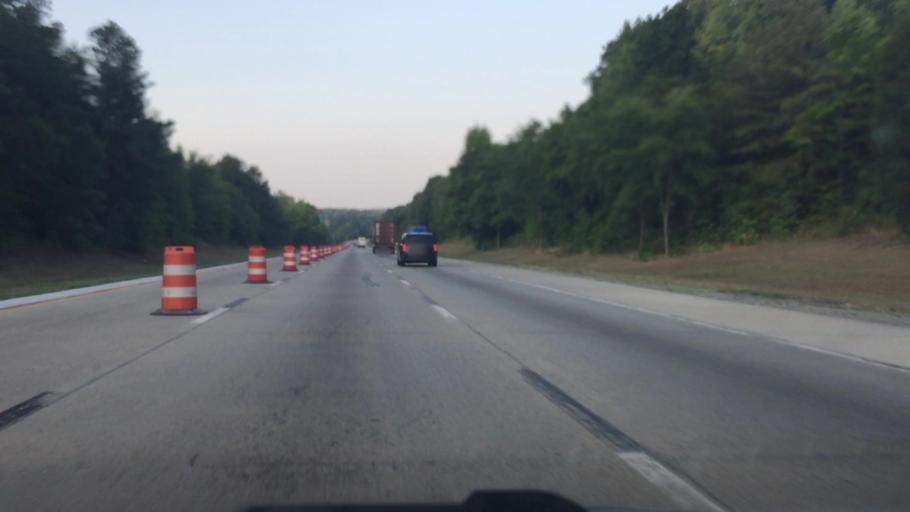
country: US
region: North Carolina
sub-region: Guilford County
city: Jamestown
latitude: 35.9513
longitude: -79.8995
